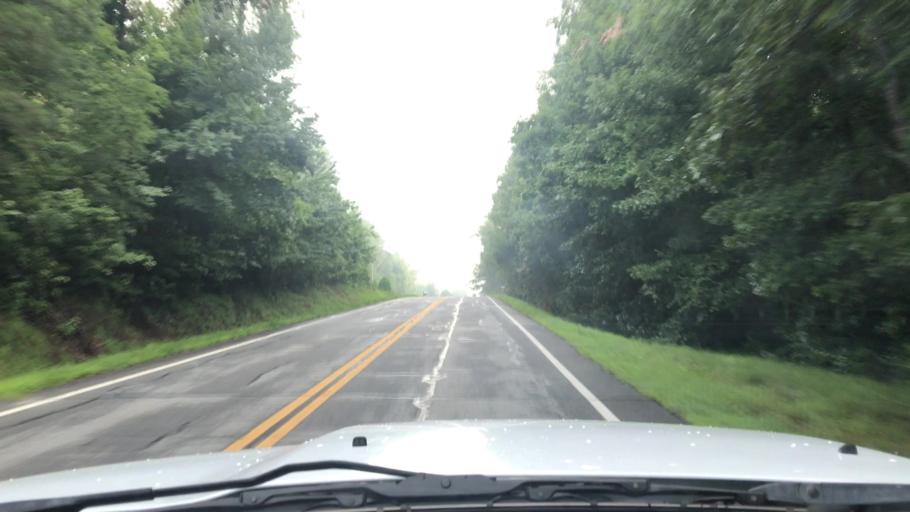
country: US
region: Georgia
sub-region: Fannin County
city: Blue Ridge
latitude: 34.9678
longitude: -84.2133
